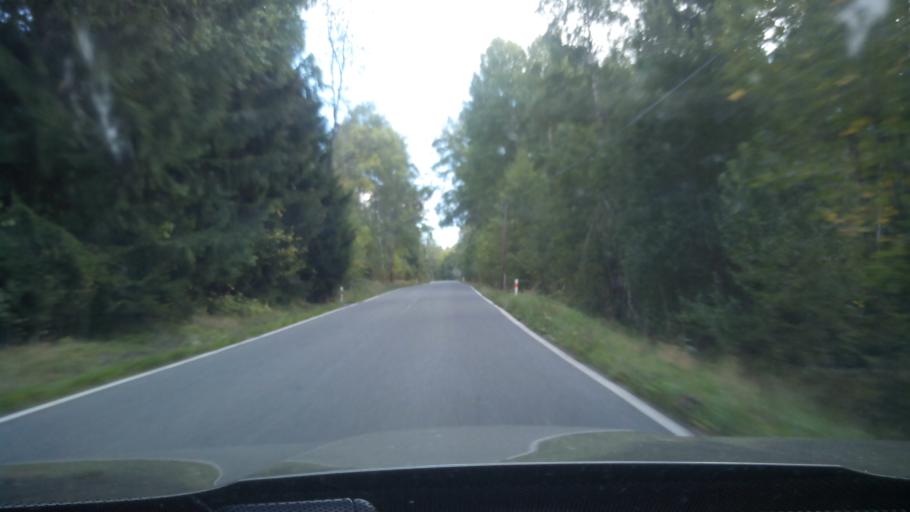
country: CZ
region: Plzensky
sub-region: Okres Klatovy
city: Kasperske Hory
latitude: 49.1390
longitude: 13.5792
